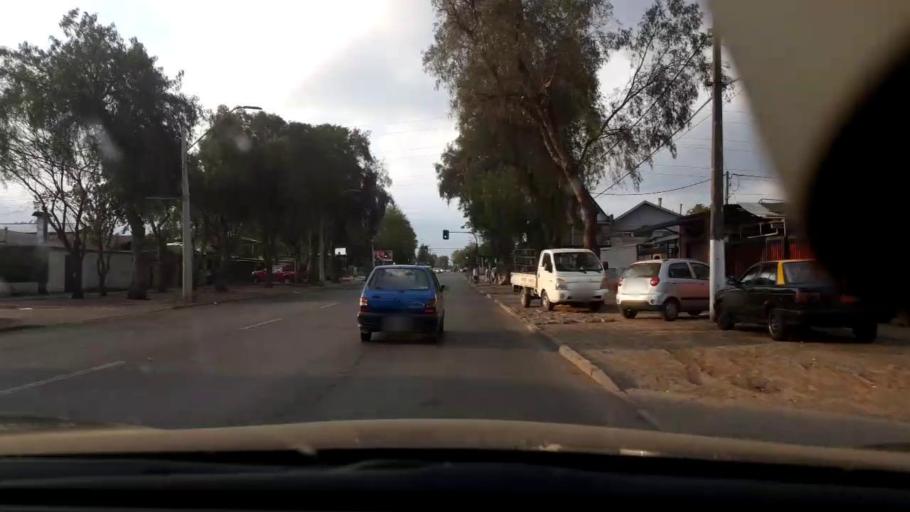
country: CL
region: Santiago Metropolitan
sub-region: Provincia de Santiago
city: Lo Prado
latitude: -33.4233
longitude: -70.7517
